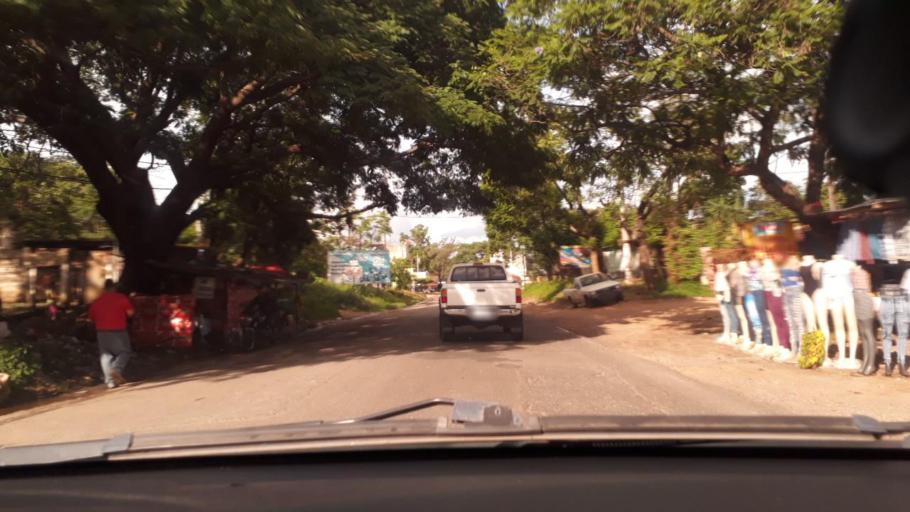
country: GT
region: Jutiapa
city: Jutiapa
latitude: 14.2911
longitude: -89.9238
